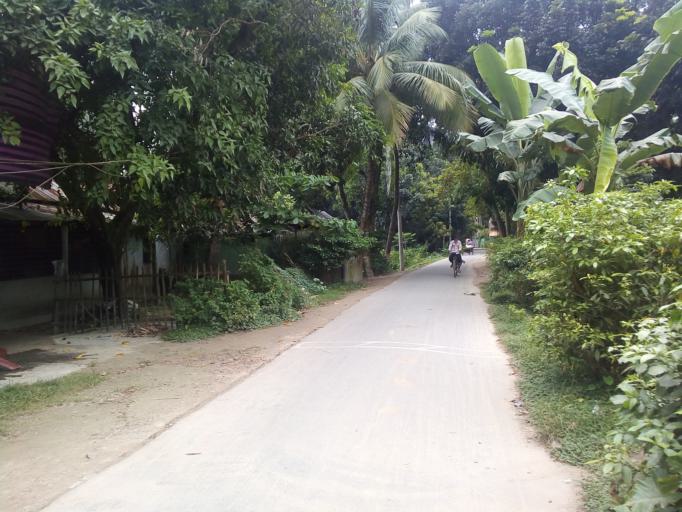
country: BD
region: Dhaka
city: Faridpur
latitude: 23.5484
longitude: 89.6298
